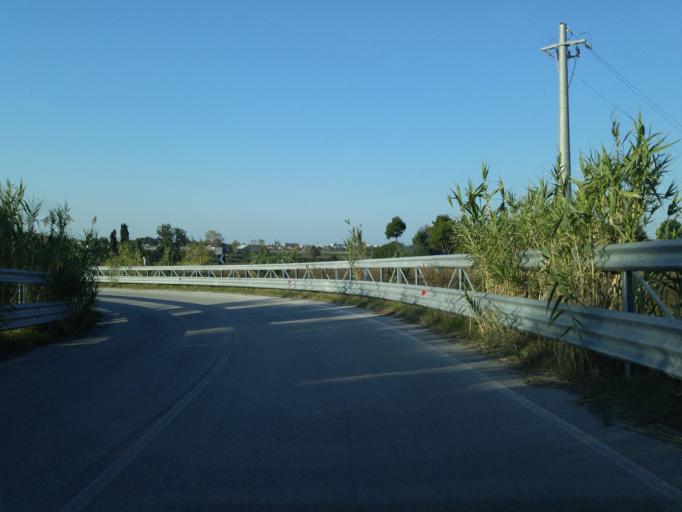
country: IT
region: The Marches
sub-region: Provincia di Pesaro e Urbino
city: Fano
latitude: 43.8143
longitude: 13.0291
